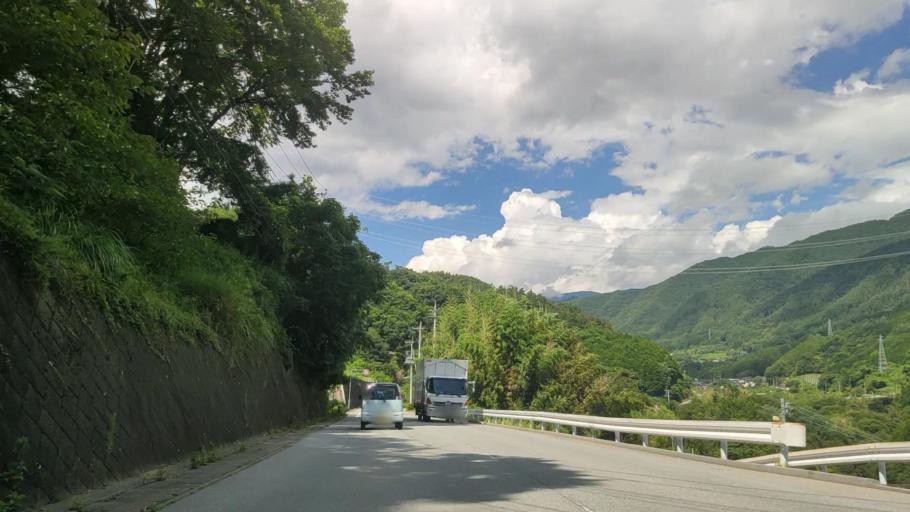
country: JP
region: Yamanashi
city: Enzan
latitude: 35.7566
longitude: 138.7268
